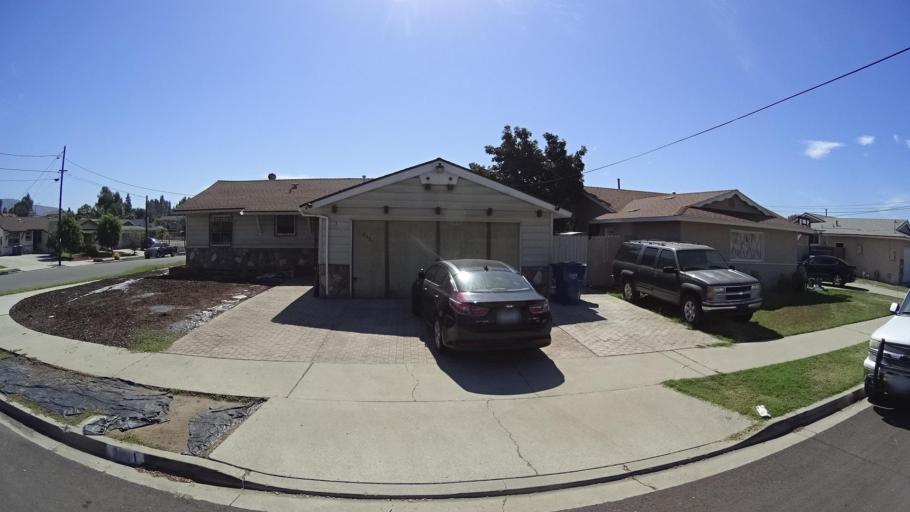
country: US
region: California
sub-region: San Diego County
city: La Presa
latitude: 32.7085
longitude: -117.0047
